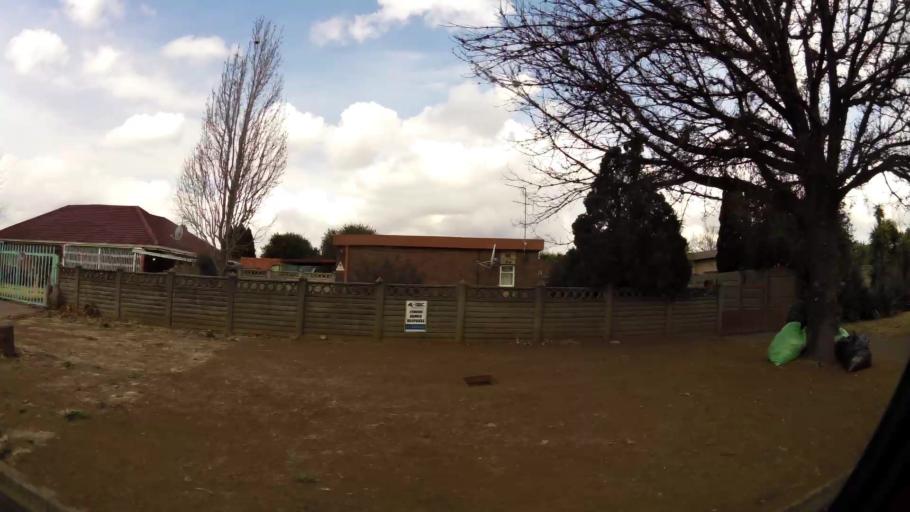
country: ZA
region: Gauteng
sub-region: Sedibeng District Municipality
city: Vanderbijlpark
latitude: -26.7200
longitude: 27.8492
